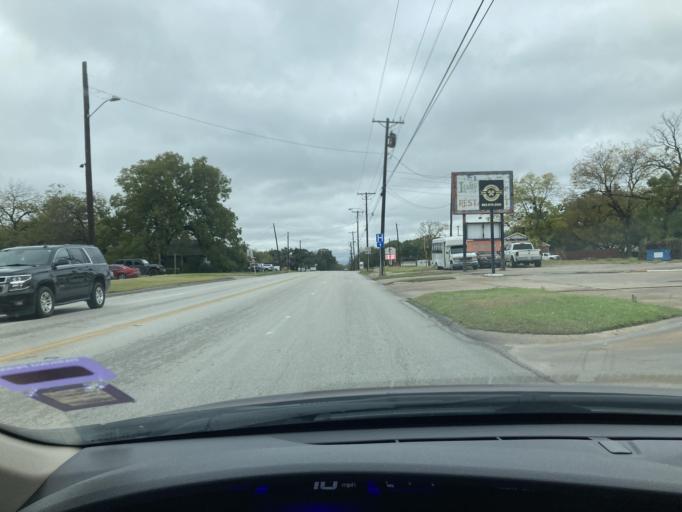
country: US
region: Texas
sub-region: Navarro County
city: Corsicana
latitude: 32.0896
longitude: -96.4817
